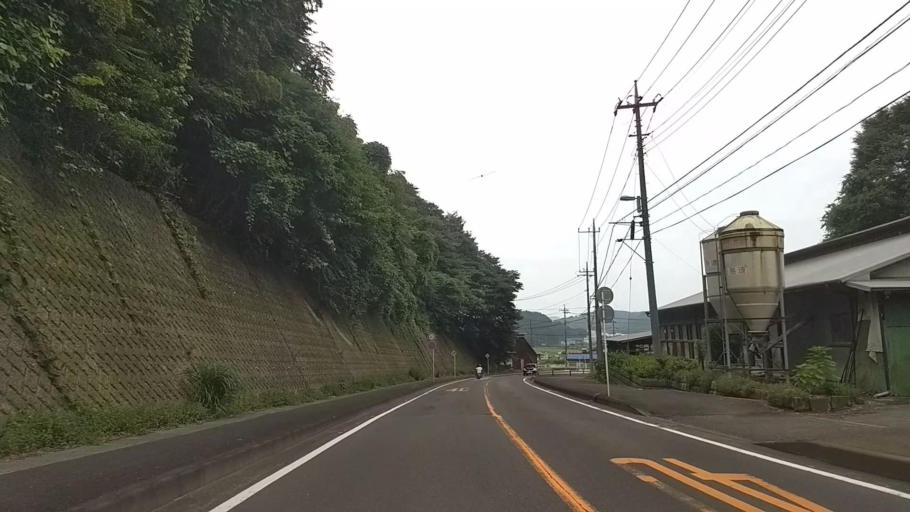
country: JP
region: Kanagawa
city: Hadano
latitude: 35.3334
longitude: 139.2200
